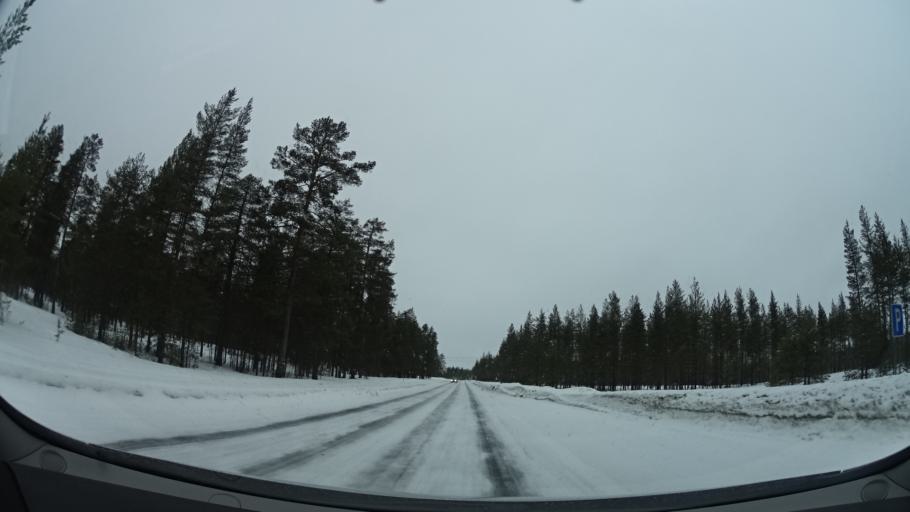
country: SE
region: Vaesterbotten
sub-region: Mala Kommun
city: Mala
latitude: 65.1350
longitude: 18.8657
